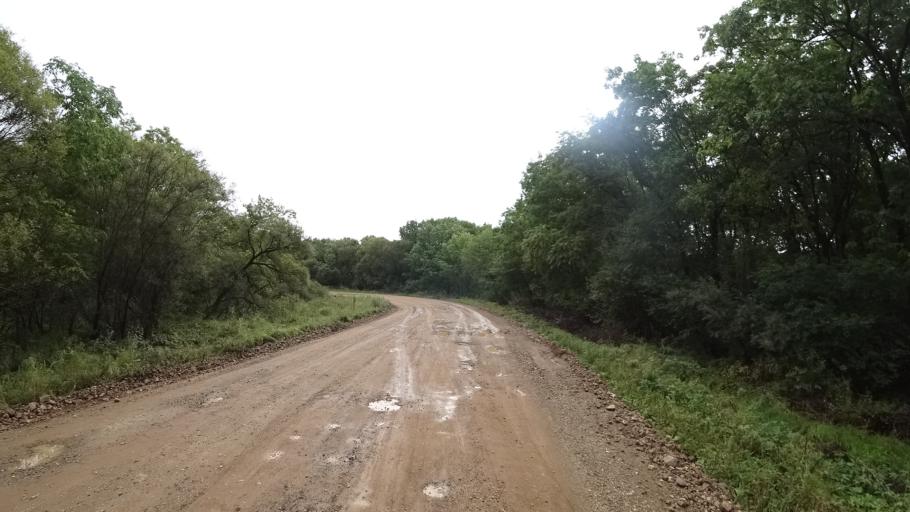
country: RU
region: Primorskiy
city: Lyalichi
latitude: 44.0799
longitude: 132.4509
